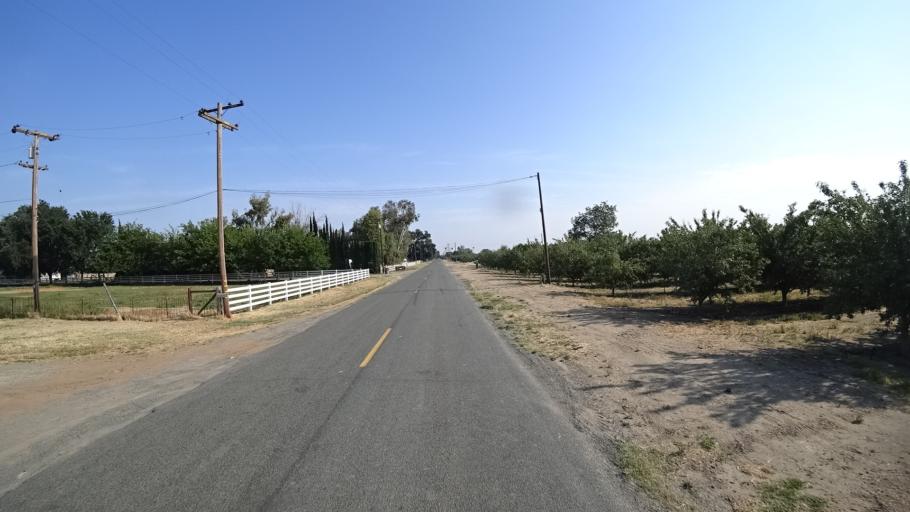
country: US
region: California
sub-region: Kings County
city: Lemoore
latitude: 36.3624
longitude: -119.8251
